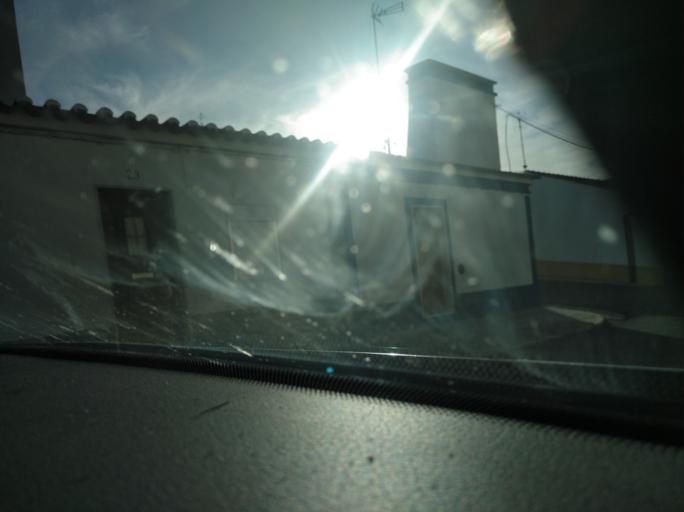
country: PT
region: Evora
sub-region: Estremoz
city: Estremoz
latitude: 38.9512
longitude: -7.4989
